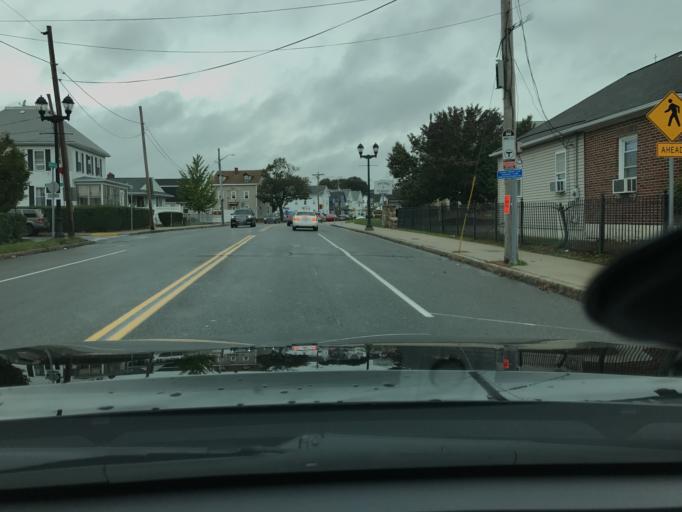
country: US
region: Massachusetts
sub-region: Essex County
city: Peabody
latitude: 42.5322
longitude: -70.9123
